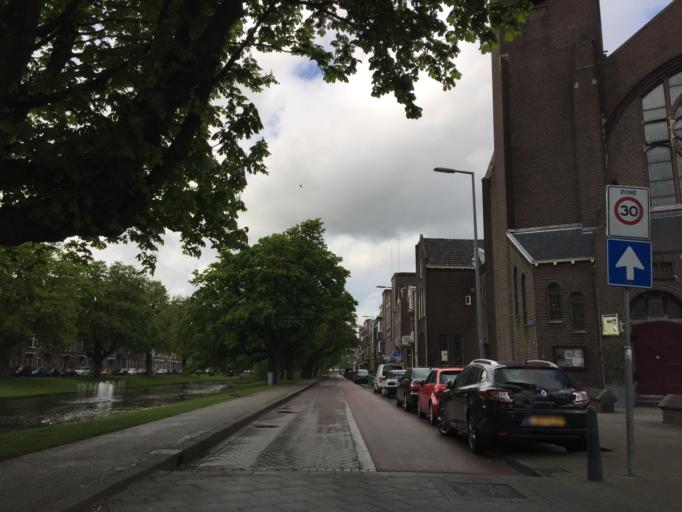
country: NL
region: South Holland
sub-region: Gemeente Rotterdam
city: Rotterdam
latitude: 51.9353
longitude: 4.4703
